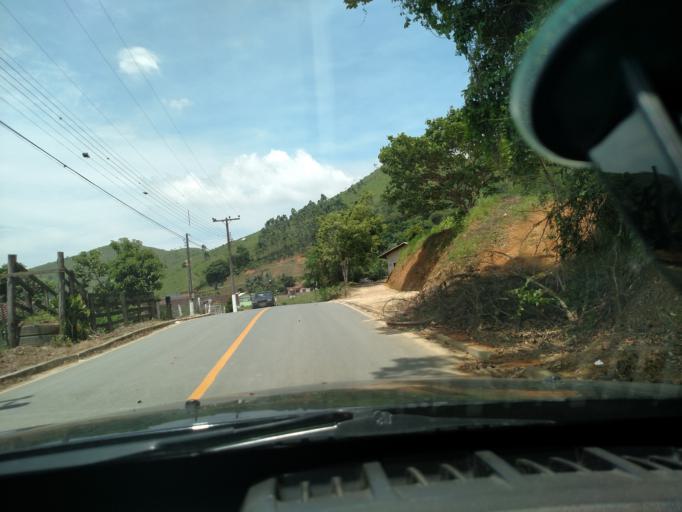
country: BR
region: Santa Catarina
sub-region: Gaspar
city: Gaspar
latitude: -26.9128
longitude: -48.8142
